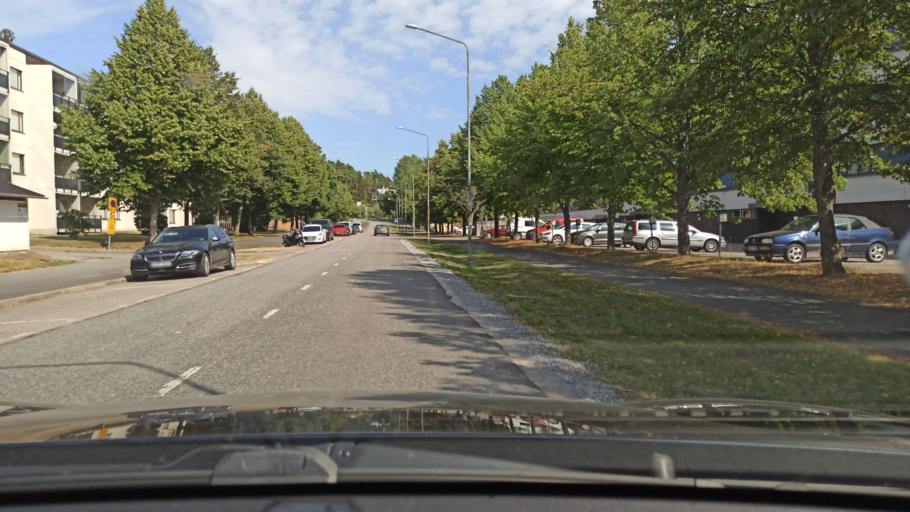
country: FI
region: Uusimaa
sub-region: Helsinki
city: Kirkkonummi
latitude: 60.1304
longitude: 24.4270
